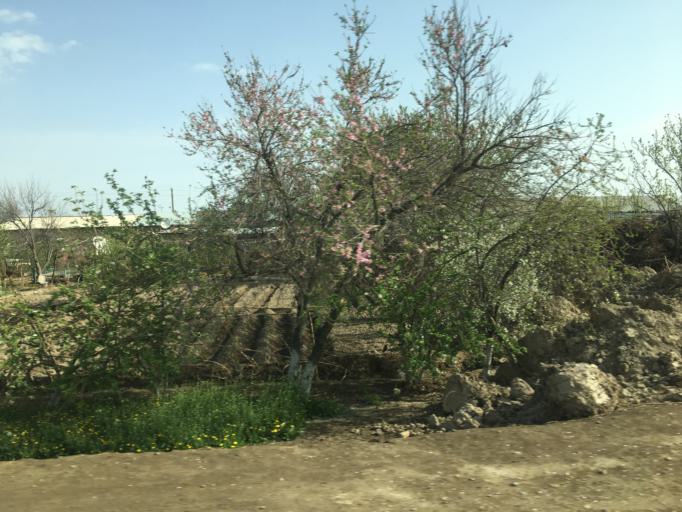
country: TM
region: Mary
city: Seydi
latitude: 39.3031
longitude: 63.0319
